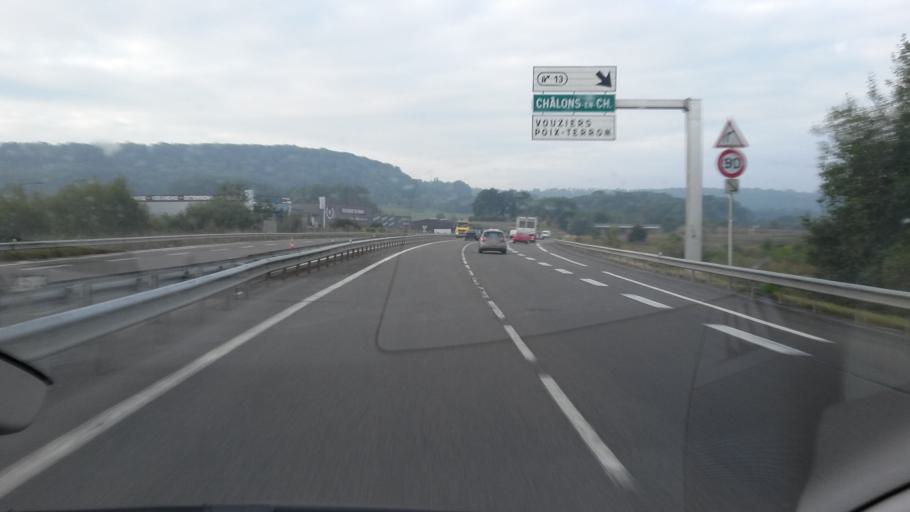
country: FR
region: Champagne-Ardenne
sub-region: Departement des Ardennes
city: La Francheville
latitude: 49.6458
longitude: 4.6301
